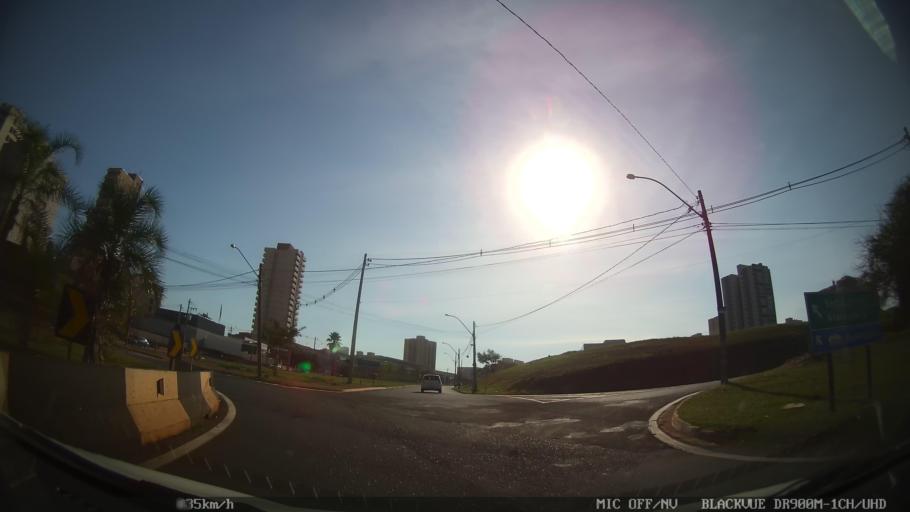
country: BR
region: Sao Paulo
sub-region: Ribeirao Preto
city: Ribeirao Preto
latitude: -21.2195
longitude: -47.8270
